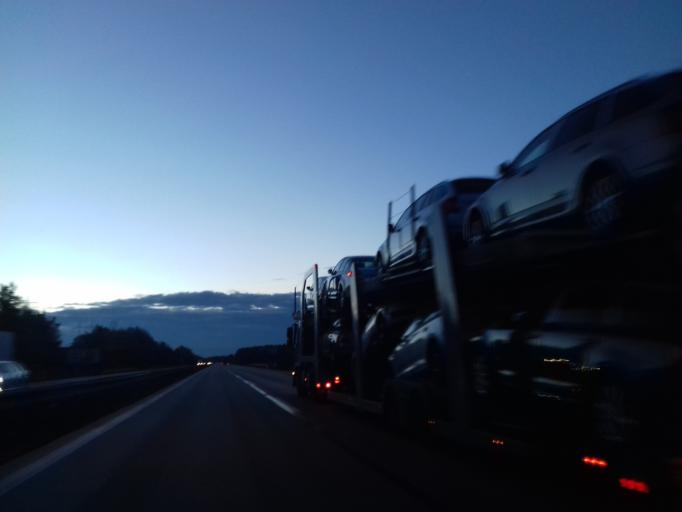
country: CZ
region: South Moravian
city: Ricany
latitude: 49.2510
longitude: 16.3539
